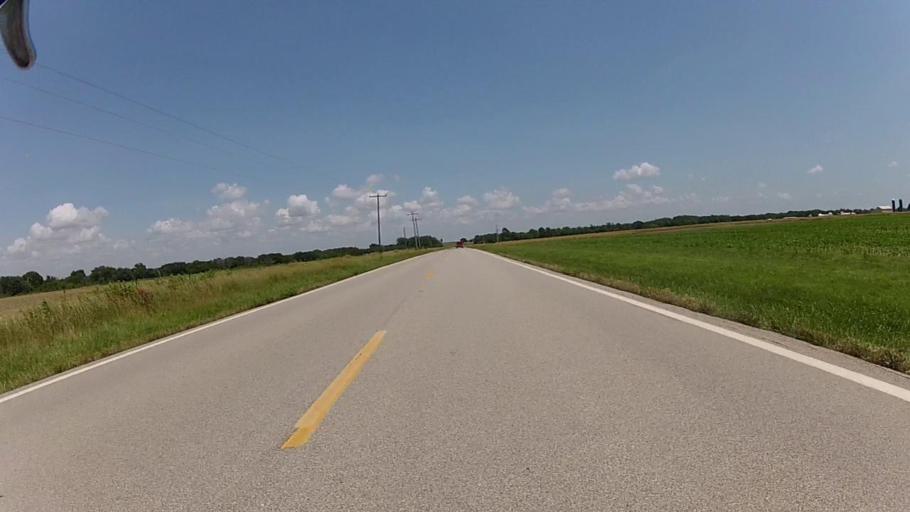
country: US
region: Kansas
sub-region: Montgomery County
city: Cherryvale
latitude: 37.1928
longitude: -95.4570
